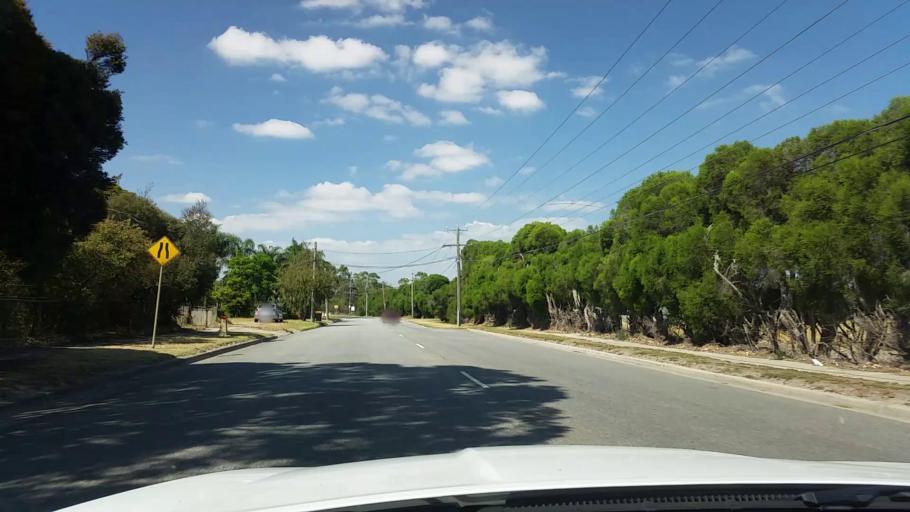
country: AU
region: Victoria
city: Heatherton
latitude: -37.9593
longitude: 145.1015
